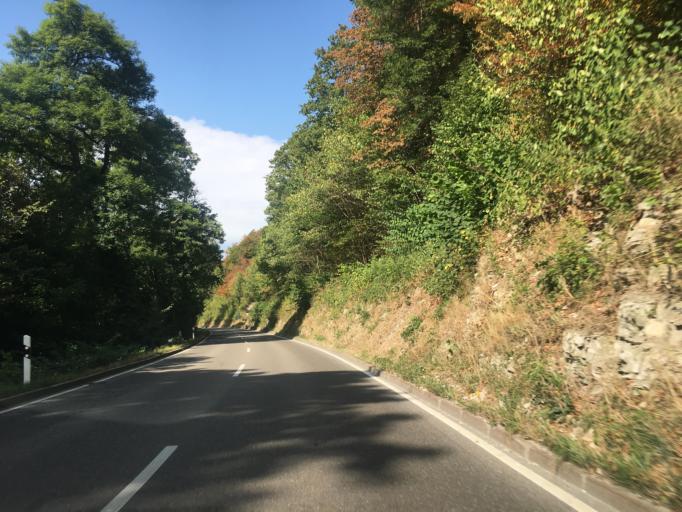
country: DE
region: Baden-Wuerttemberg
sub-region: Tuebingen Region
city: Pfullingen
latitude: 48.4188
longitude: 9.1812
